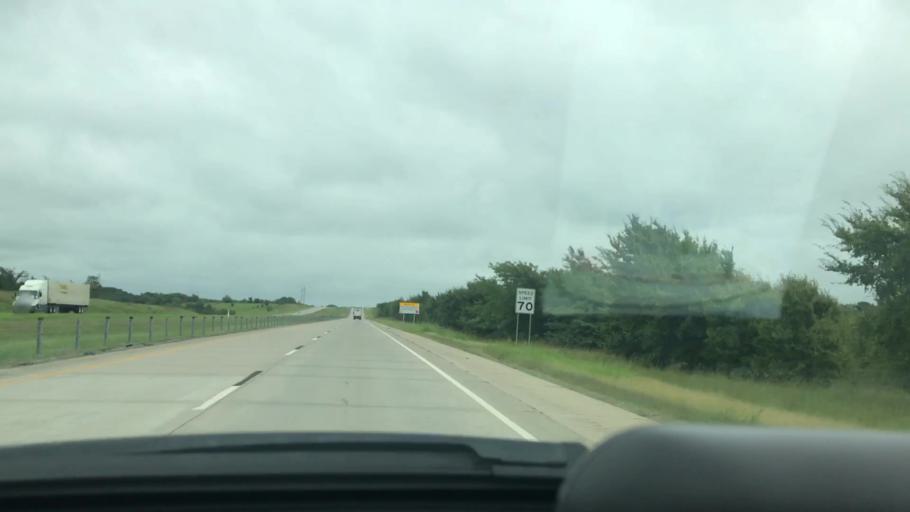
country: US
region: Oklahoma
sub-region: Pittsburg County
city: McAlester
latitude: 34.6838
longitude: -95.9237
